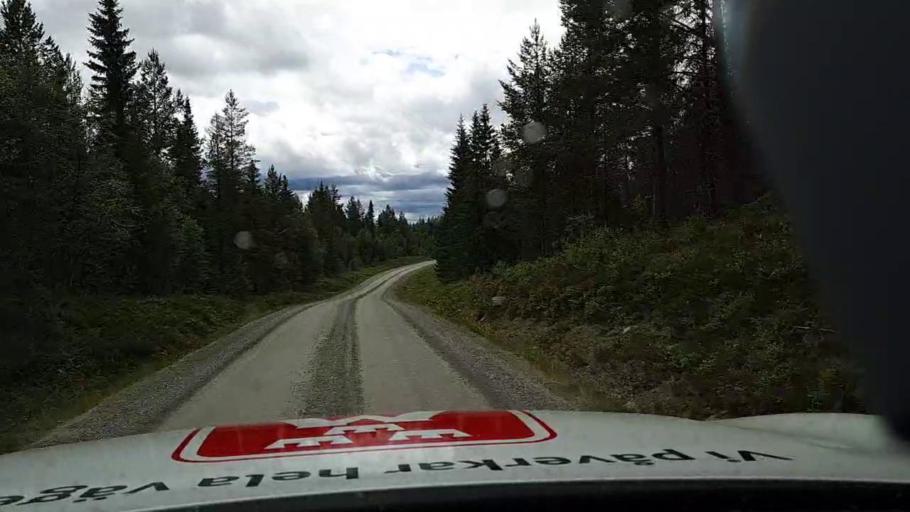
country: SE
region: Jaemtland
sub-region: Are Kommun
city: Jarpen
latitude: 62.8284
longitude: 13.8203
